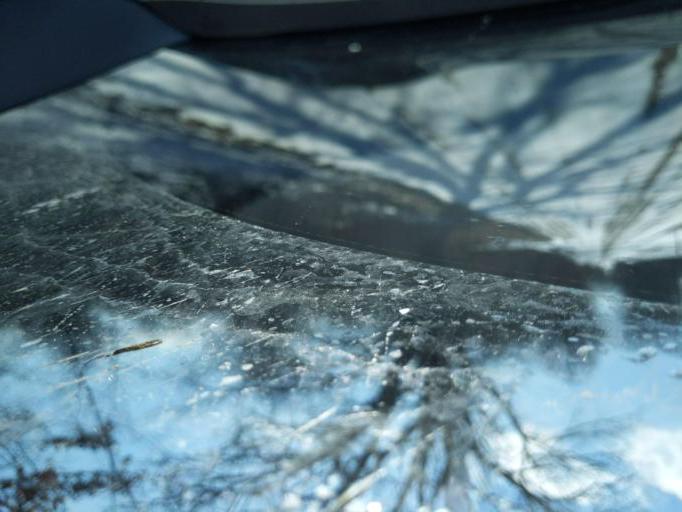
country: US
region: Michigan
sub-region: Ingham County
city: Stockbridge
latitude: 42.5333
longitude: -84.0880
